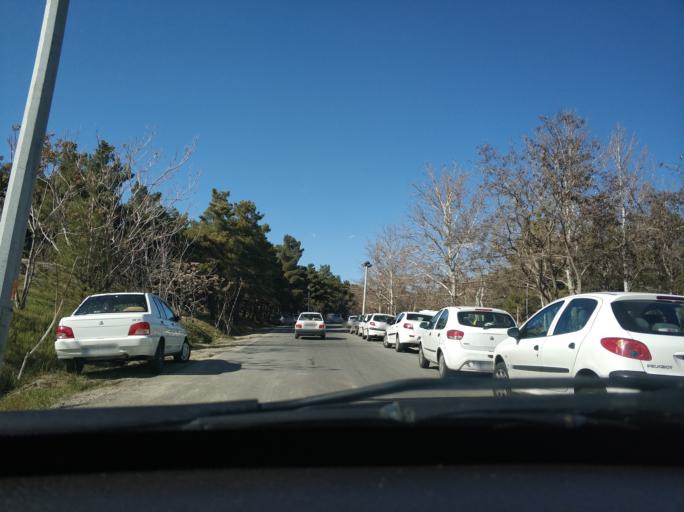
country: IR
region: Tehran
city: Tajrish
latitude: 35.7847
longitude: 51.5581
